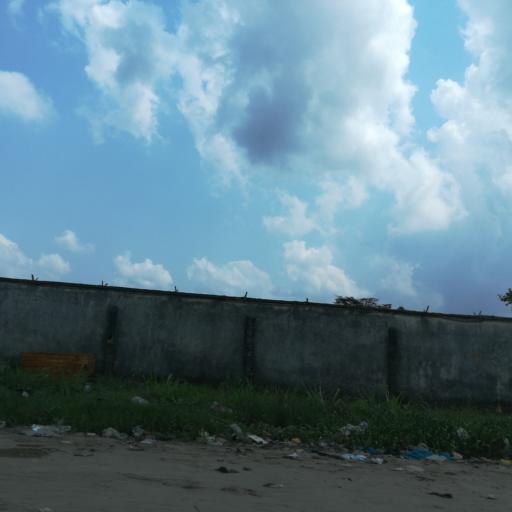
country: NG
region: Rivers
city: Okrika
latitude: 4.8176
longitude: 7.0945
